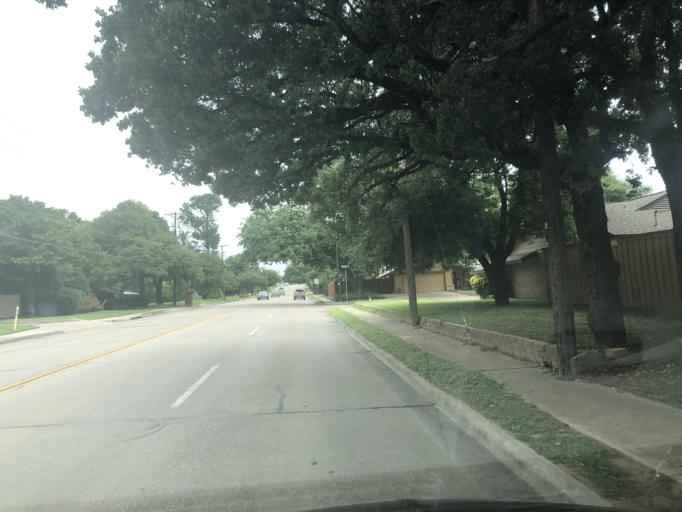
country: US
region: Texas
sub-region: Dallas County
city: Irving
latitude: 32.7962
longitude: -96.9770
